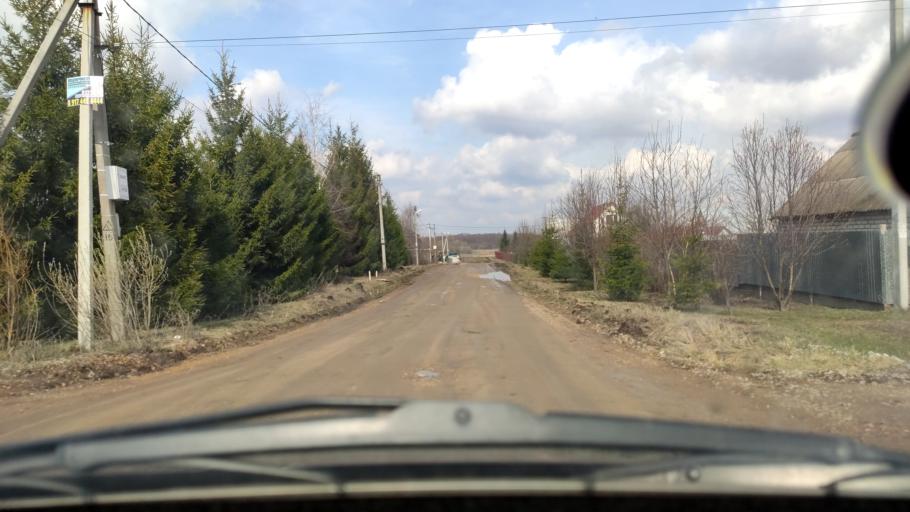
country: RU
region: Bashkortostan
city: Iglino
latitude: 54.7982
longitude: 56.2755
